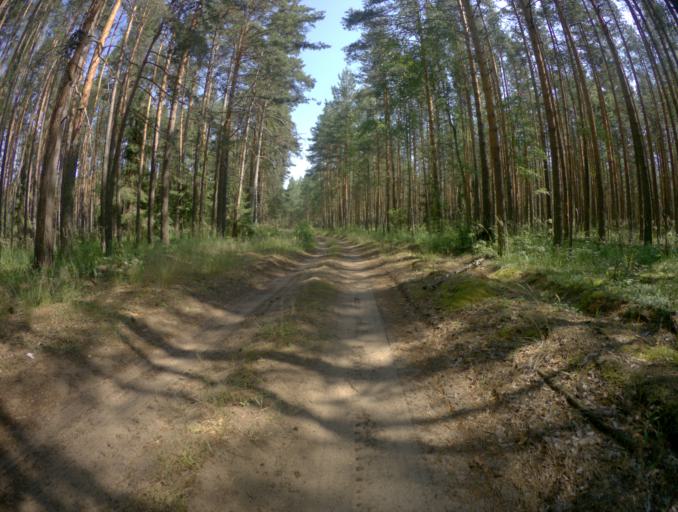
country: RU
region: Ivanovo
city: Talitsy
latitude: 56.3936
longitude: 42.2588
